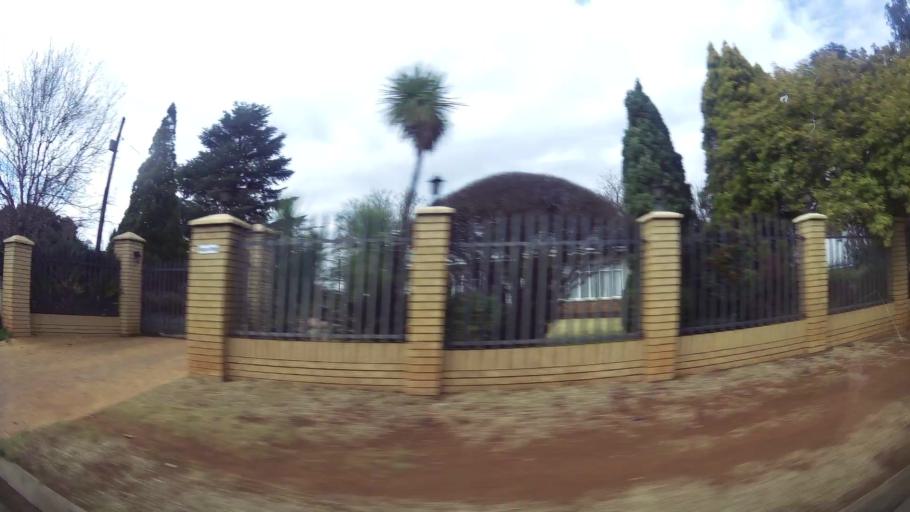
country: ZA
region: Gauteng
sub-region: Sedibeng District Municipality
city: Meyerton
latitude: -26.5950
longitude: 27.9930
